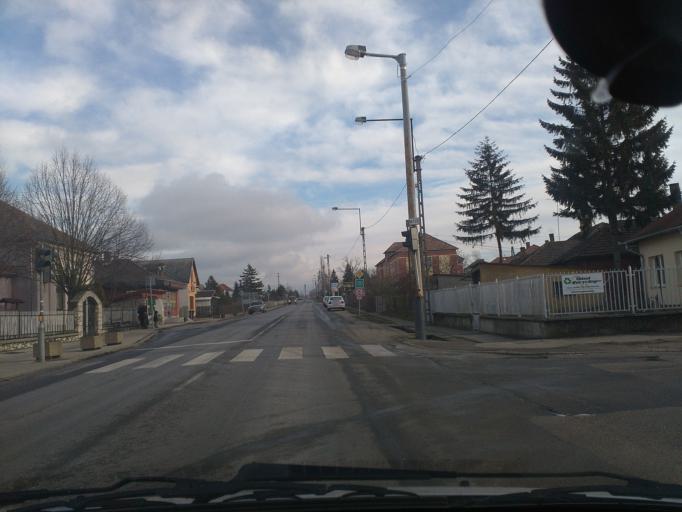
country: HU
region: Komarom-Esztergom
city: Tokod
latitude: 47.7326
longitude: 18.6885
